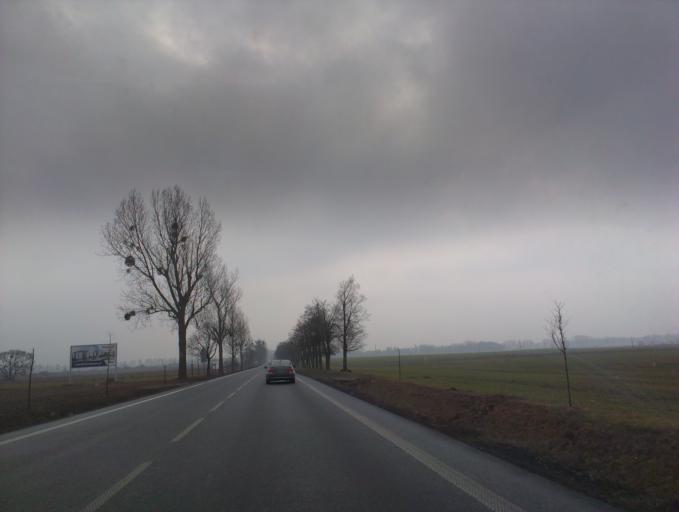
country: PL
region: Greater Poland Voivodeship
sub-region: Powiat obornicki
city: Oborniki
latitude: 52.6156
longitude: 16.8136
